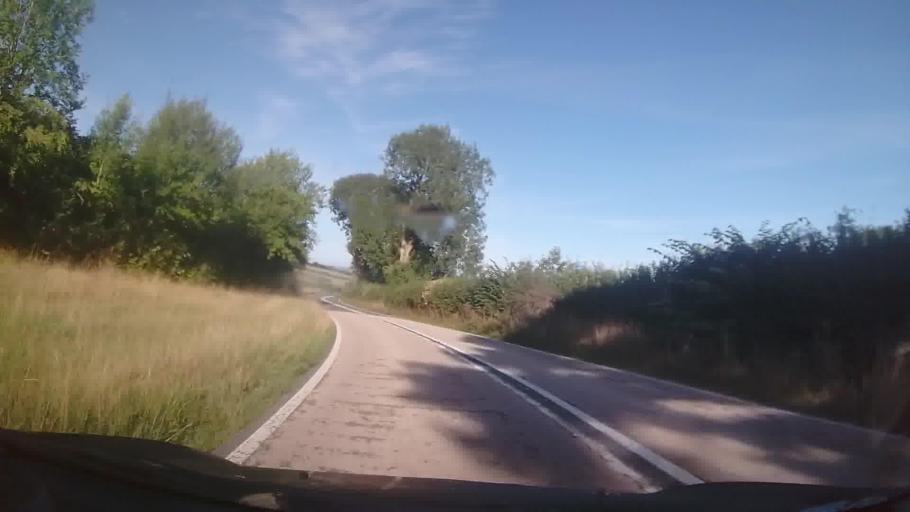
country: GB
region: Wales
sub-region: Sir Powys
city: Hay
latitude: 51.9645
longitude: -3.2072
